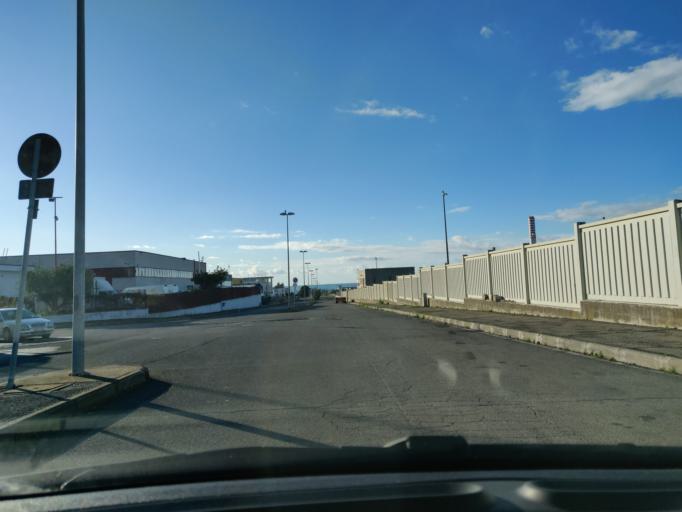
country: IT
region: Latium
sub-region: Citta metropolitana di Roma Capitale
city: Aurelia
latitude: 42.1205
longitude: 11.7831
